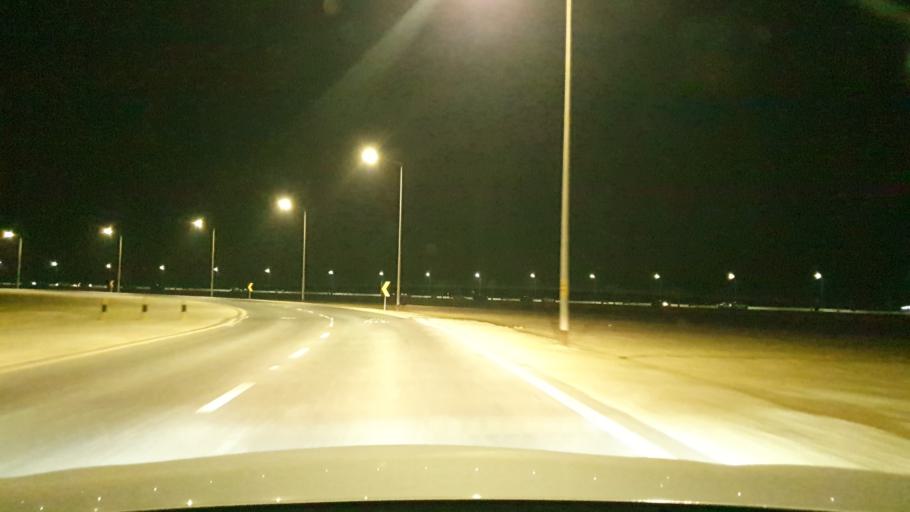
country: BH
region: Muharraq
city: Al Muharraq
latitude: 26.2851
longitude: 50.5798
